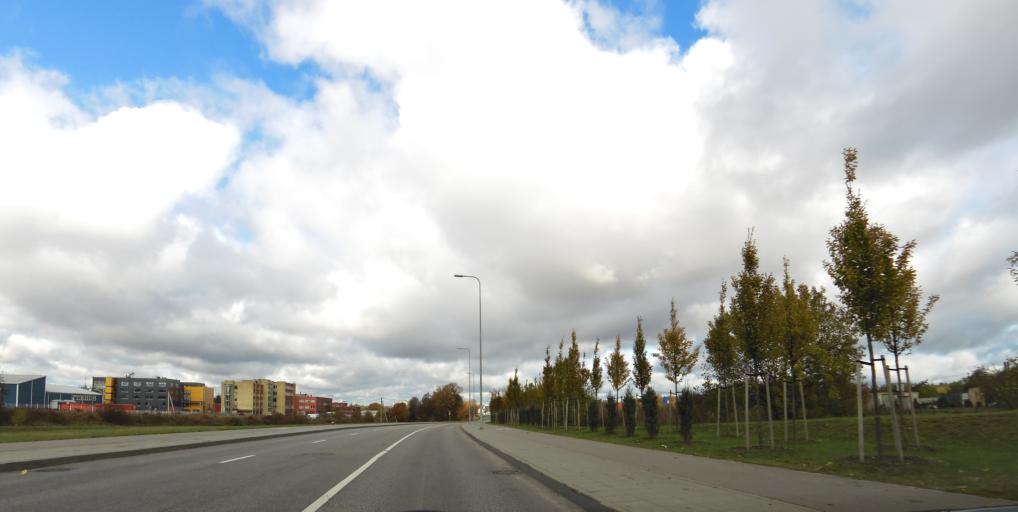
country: LT
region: Vilnius County
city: Naujamiestis
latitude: 54.6463
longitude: 25.2765
